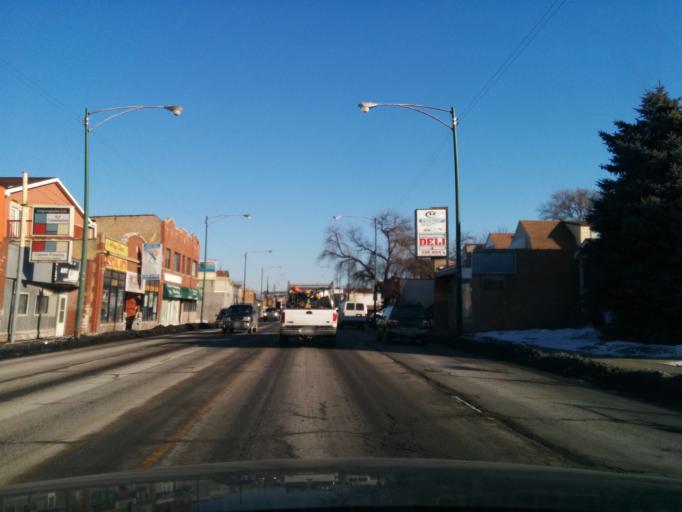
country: US
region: Illinois
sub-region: Cook County
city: Lincolnwood
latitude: 41.9480
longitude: -87.7471
